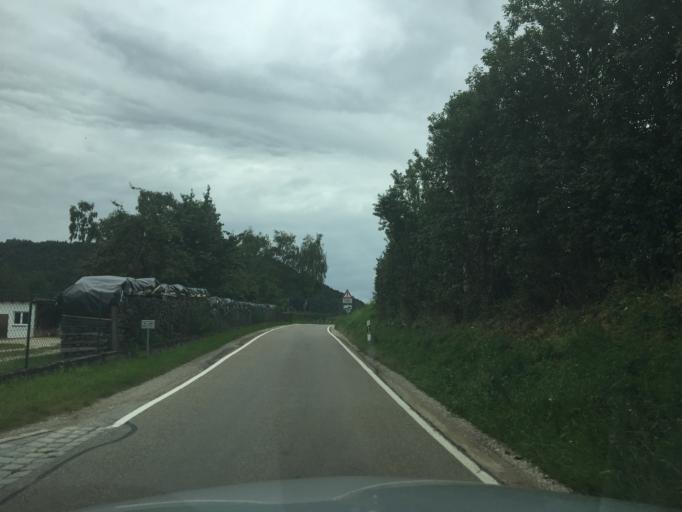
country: DE
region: Bavaria
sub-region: Regierungsbezirk Mittelfranken
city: Greding
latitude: 49.0304
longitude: 11.3682
